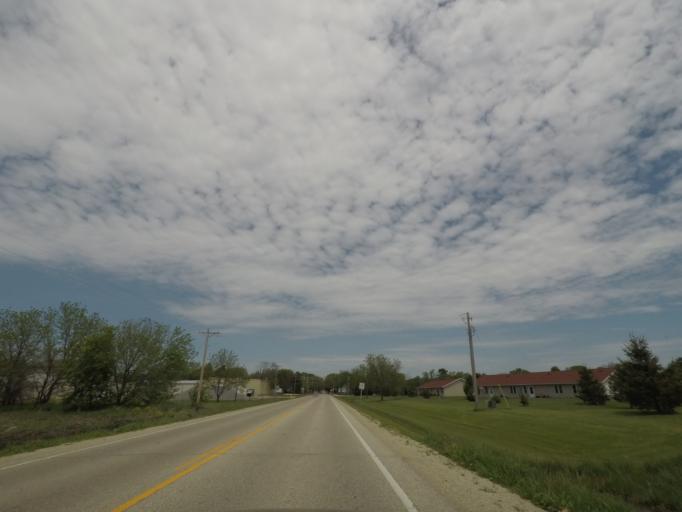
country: US
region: Wisconsin
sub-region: Rock County
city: Evansville
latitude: 42.7704
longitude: -89.2990
